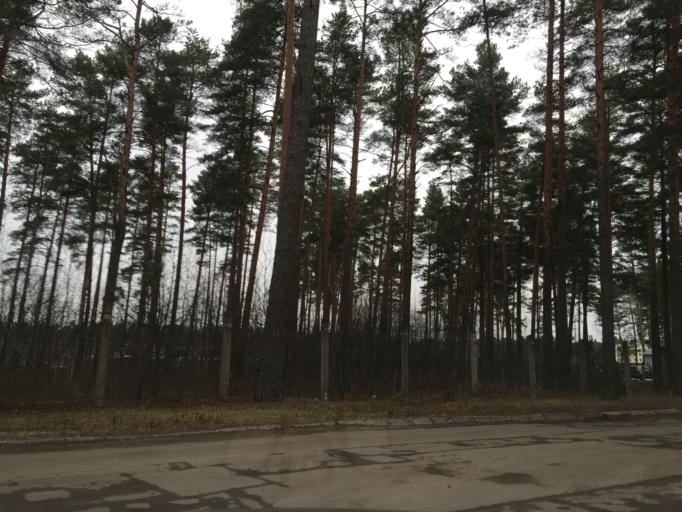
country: LV
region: Garkalne
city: Garkalne
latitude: 56.9617
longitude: 24.4264
